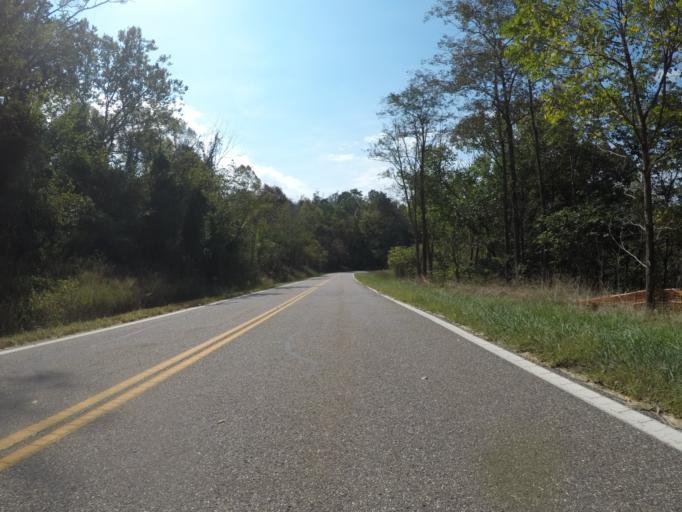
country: US
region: West Virginia
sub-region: Cabell County
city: Lesage
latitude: 38.6494
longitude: -82.4224
